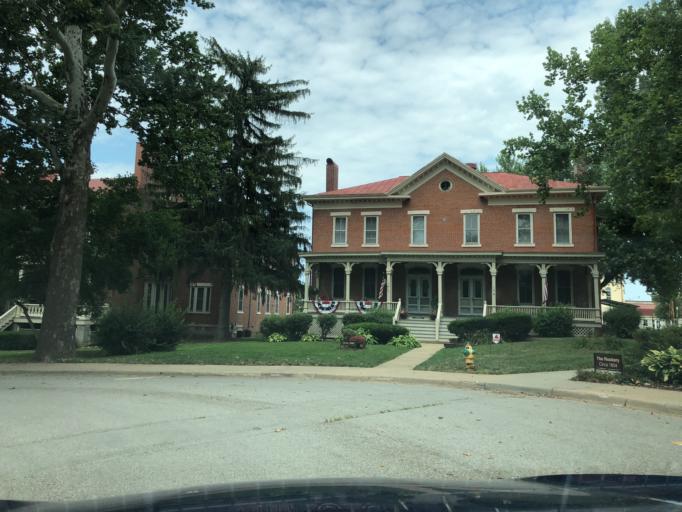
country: US
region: Kansas
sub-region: Leavenworth County
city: Leavenworth
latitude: 39.3569
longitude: -94.9175
